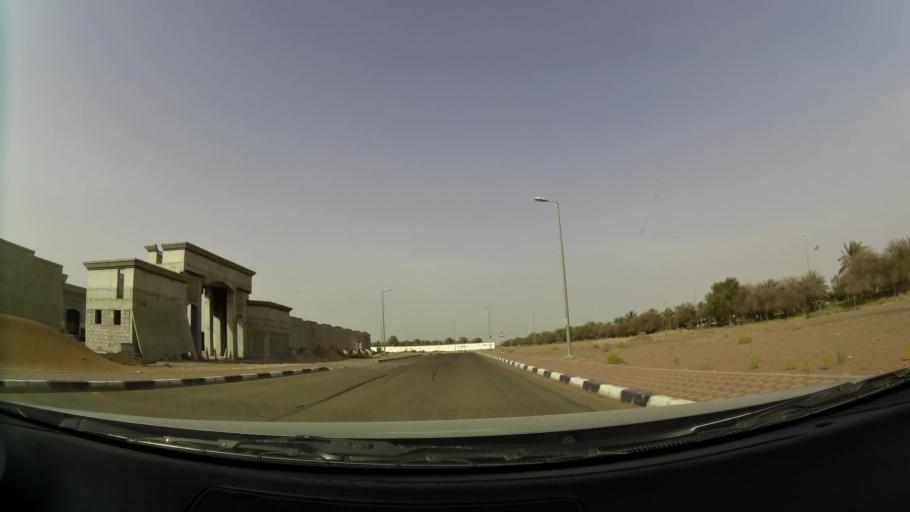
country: AE
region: Abu Dhabi
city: Al Ain
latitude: 24.1936
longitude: 55.6174
